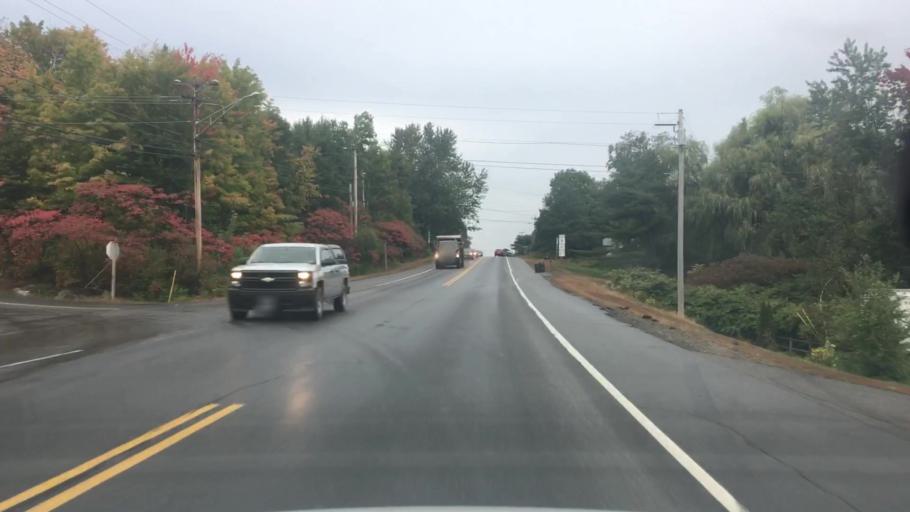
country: US
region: Maine
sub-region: Kennebec County
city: Belgrade
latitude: 44.3882
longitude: -69.8026
